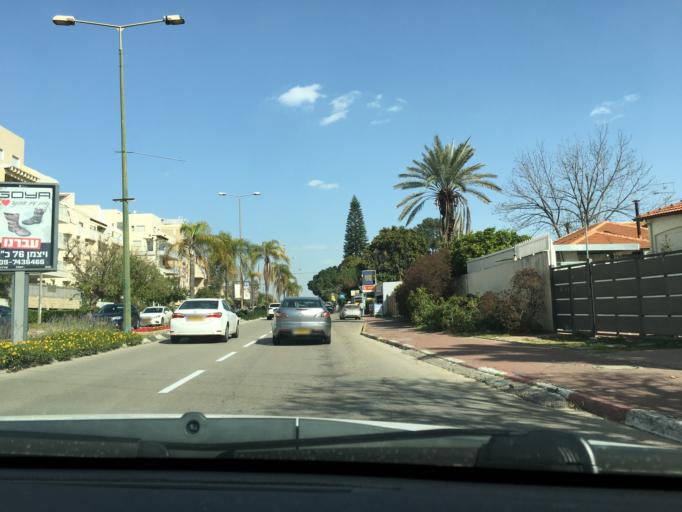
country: IL
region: Central District
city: Kfar Saba
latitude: 32.1787
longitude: 34.8952
